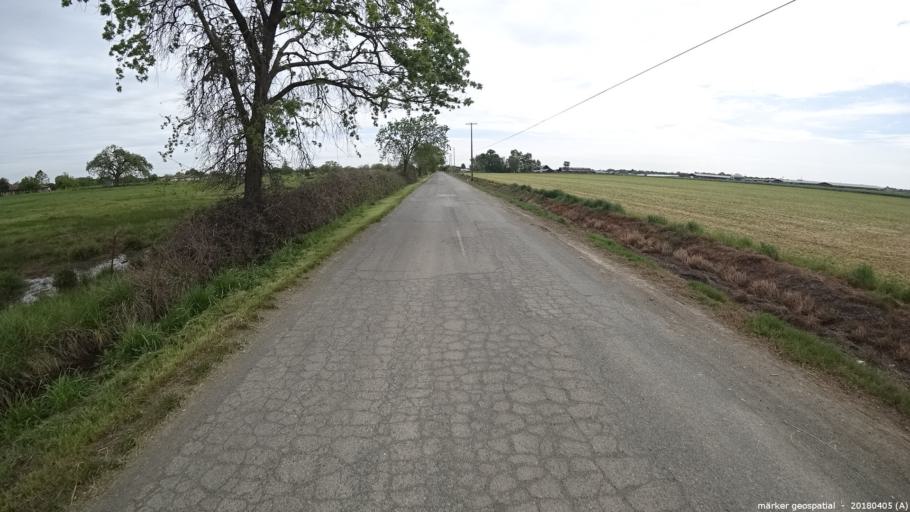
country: US
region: California
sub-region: Sacramento County
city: Galt
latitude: 38.2545
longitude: -121.3508
